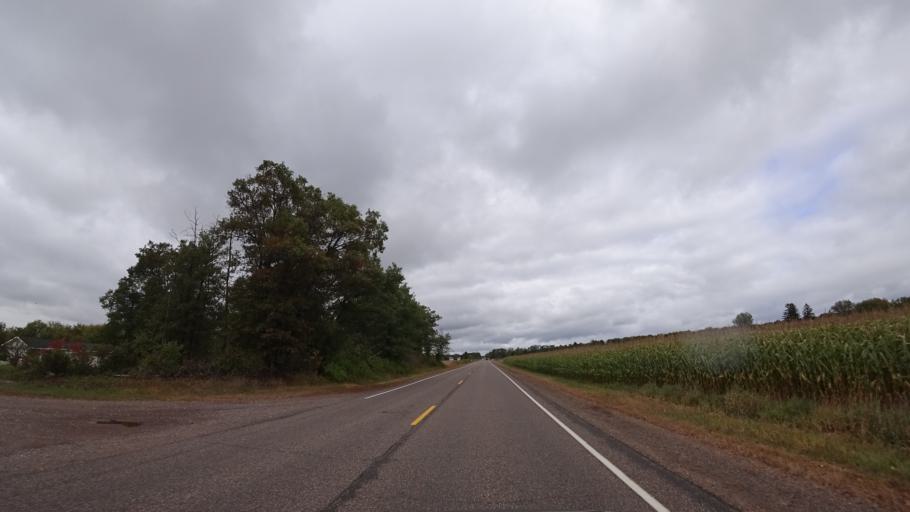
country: US
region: Wisconsin
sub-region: Chippewa County
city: Lake Wissota
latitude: 45.0113
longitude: -91.2867
